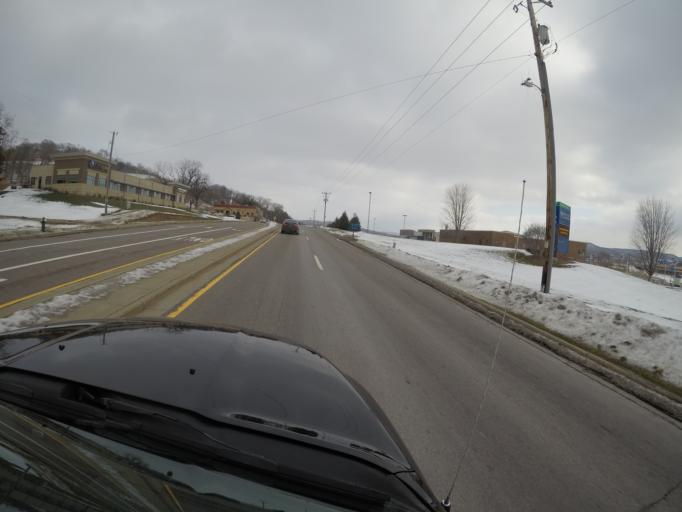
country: US
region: Wisconsin
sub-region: La Crosse County
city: Onalaska
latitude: 43.8806
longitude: -91.1992
